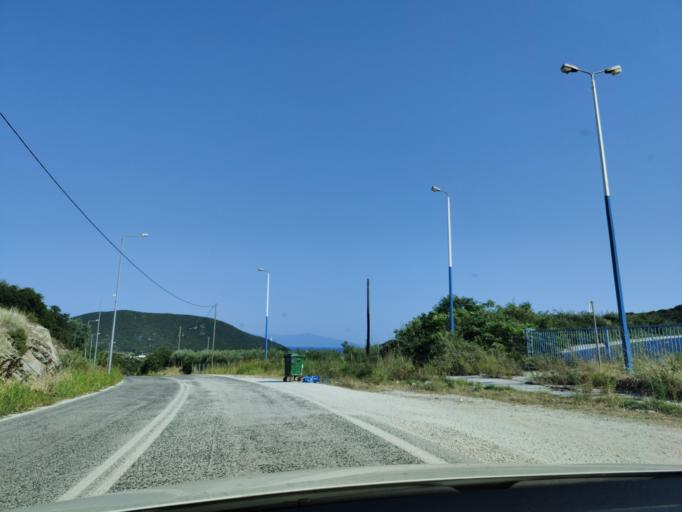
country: GR
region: East Macedonia and Thrace
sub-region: Nomos Kavalas
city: Nea Iraklitsa
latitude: 40.8592
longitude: 24.3049
